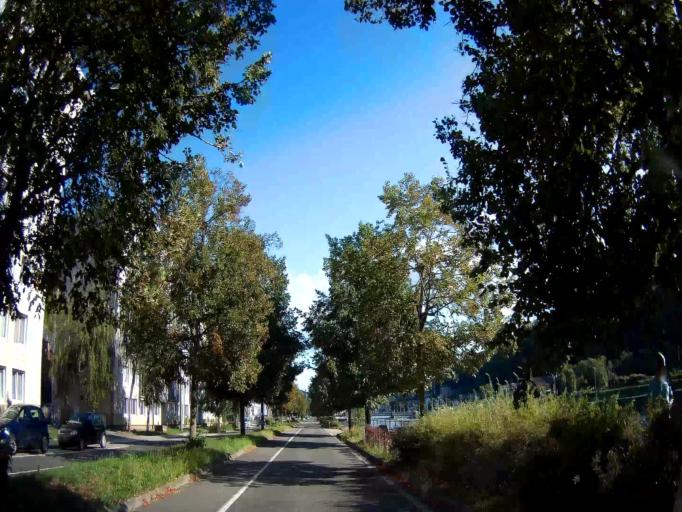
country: BE
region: Wallonia
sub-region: Province de Namur
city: Dinant
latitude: 50.2713
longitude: 4.9031
